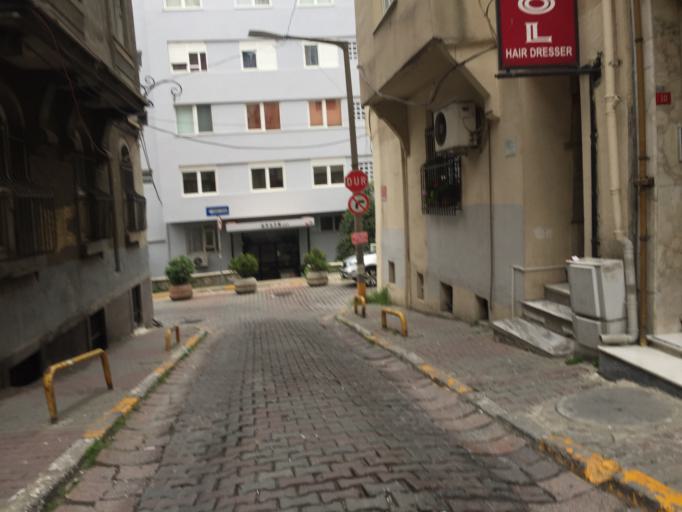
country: TR
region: Istanbul
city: Eminoenue
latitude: 41.0346
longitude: 28.9894
